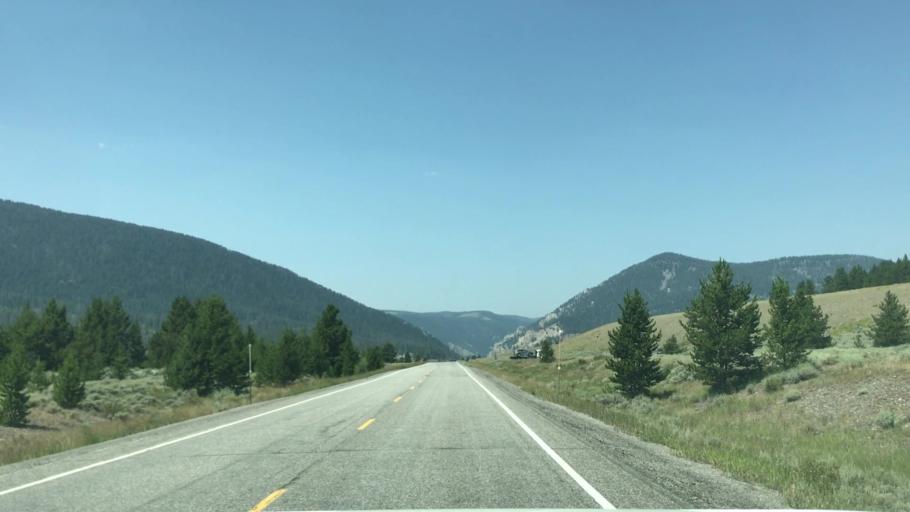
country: US
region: Montana
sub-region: Gallatin County
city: Big Sky
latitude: 45.0472
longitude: -111.1377
